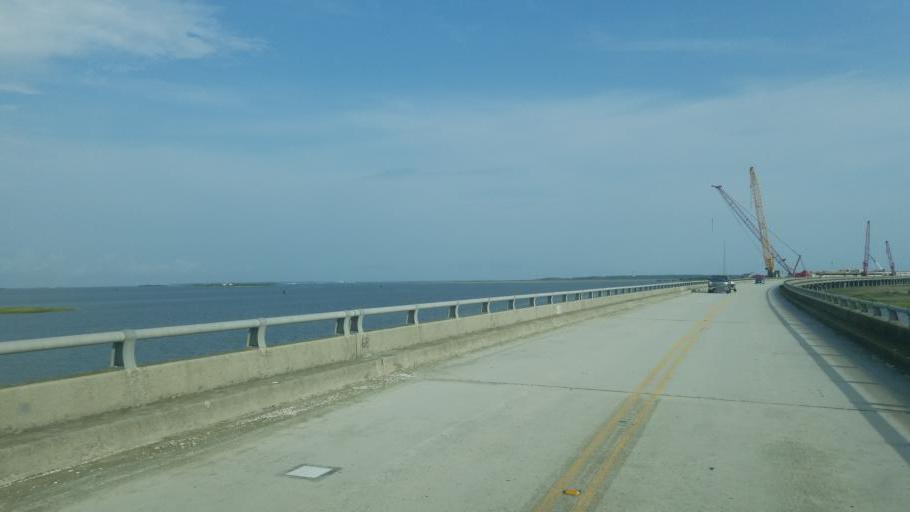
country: US
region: North Carolina
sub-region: Dare County
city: Wanchese
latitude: 35.7831
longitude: -75.5463
